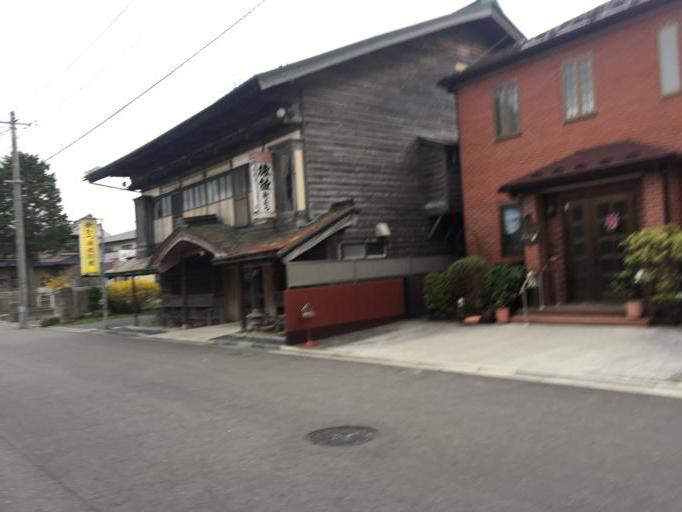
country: JP
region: Aomori
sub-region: Hachinohe Shi
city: Uchimaru
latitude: 40.5198
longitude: 141.5185
